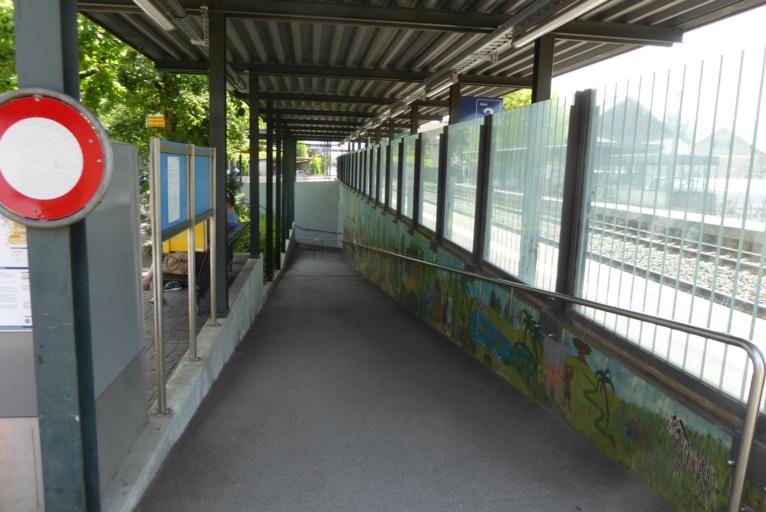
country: CH
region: Bern
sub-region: Bern-Mittelland District
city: Niederwichtrach
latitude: 46.8415
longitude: 7.5688
